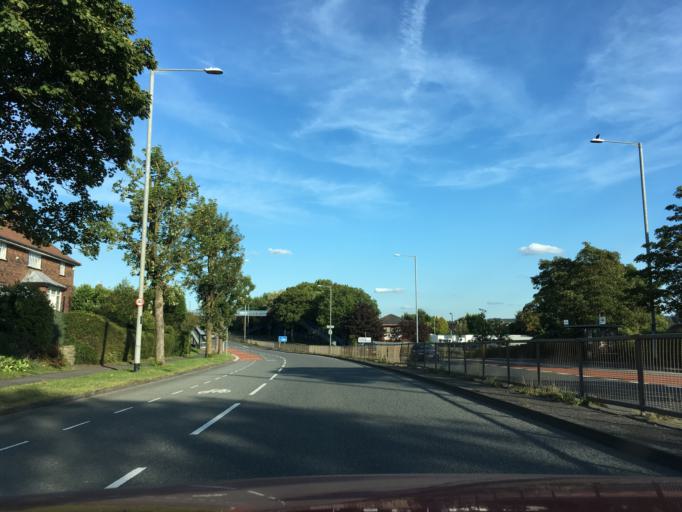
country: GB
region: England
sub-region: North Somerset
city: Easton-in-Gordano
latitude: 51.4854
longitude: -2.6812
